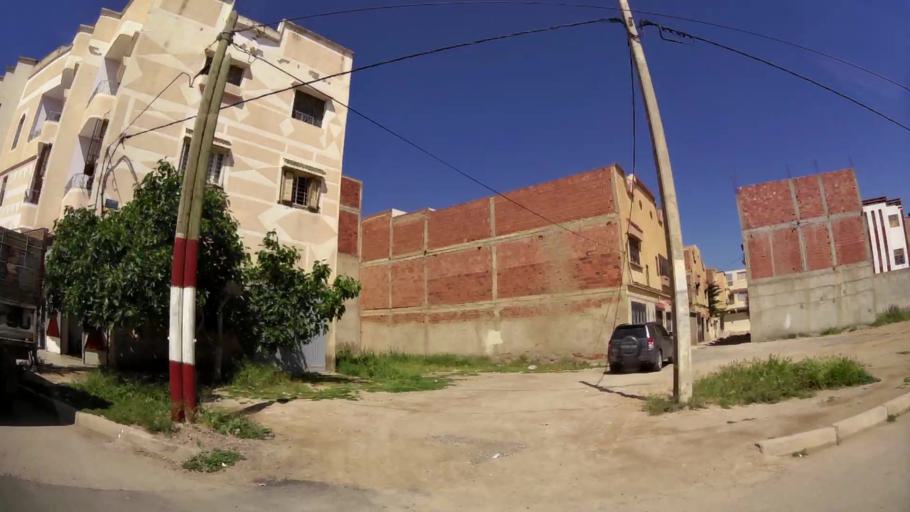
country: MA
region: Oriental
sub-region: Oujda-Angad
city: Oujda
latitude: 34.6712
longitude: -1.9409
